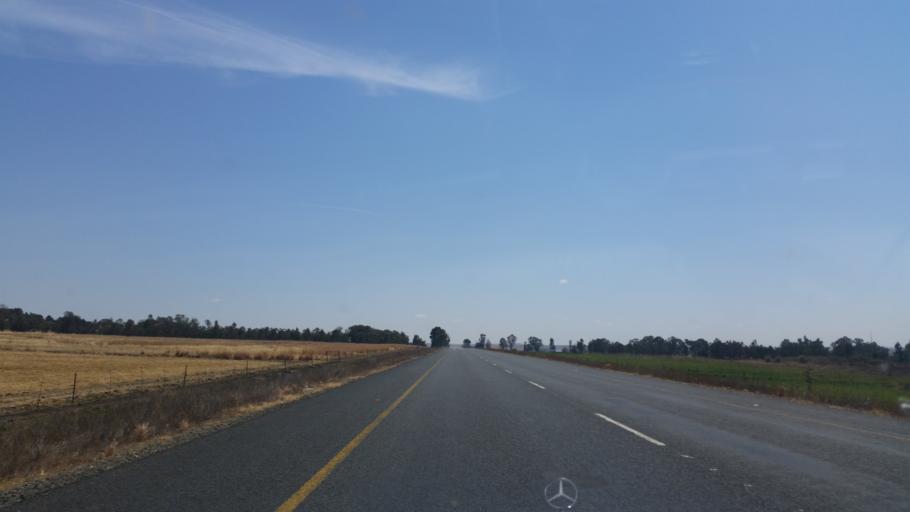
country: ZA
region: Orange Free State
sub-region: Thabo Mofutsanyana District Municipality
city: Phuthaditjhaba
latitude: -28.2176
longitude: 28.6977
